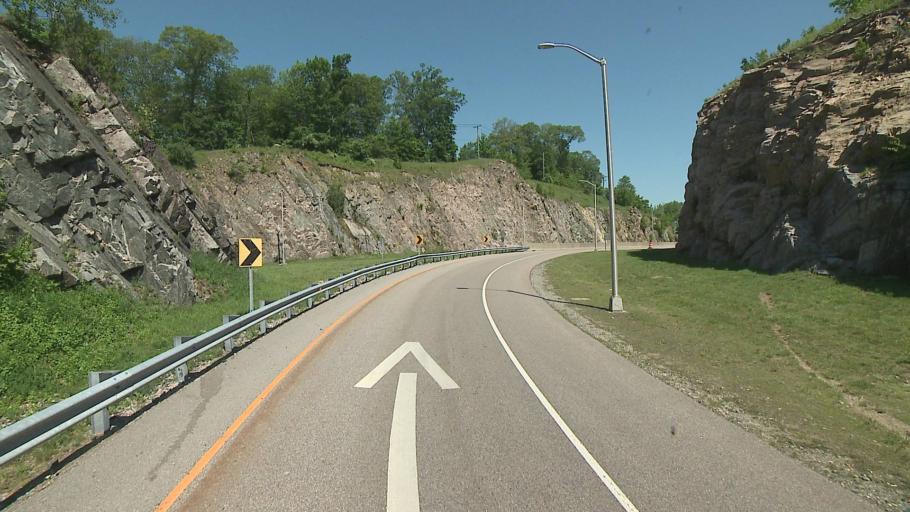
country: US
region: Connecticut
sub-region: New London County
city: Norwich
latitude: 41.4818
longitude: -72.0807
